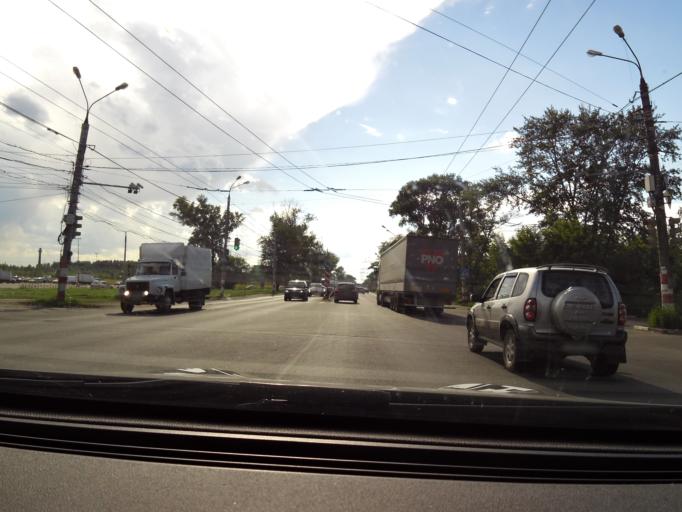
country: RU
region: Nizjnij Novgorod
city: Gorbatovka
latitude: 56.3125
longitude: 43.8408
